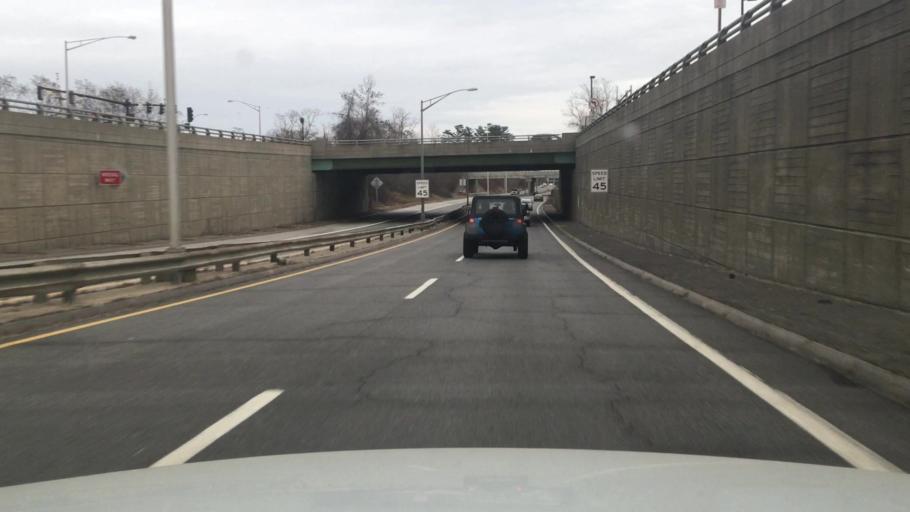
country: US
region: Maine
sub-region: Cumberland County
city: Brunswick
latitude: 43.9181
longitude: -69.9677
